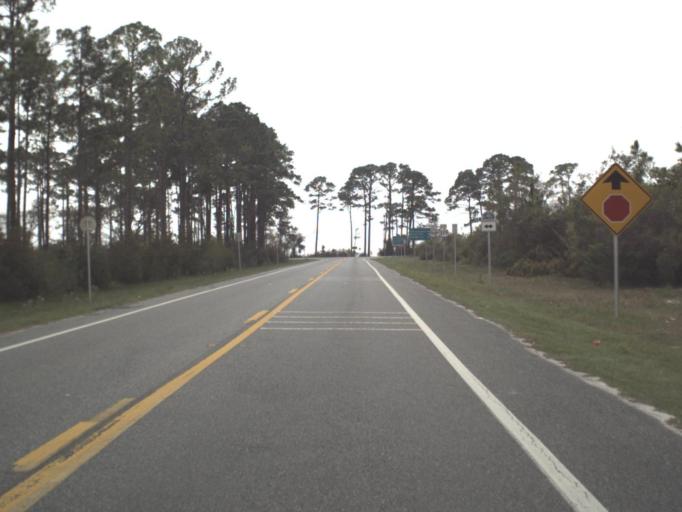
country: US
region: Florida
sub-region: Franklin County
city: Eastpoint
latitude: 29.7595
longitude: -84.8331
